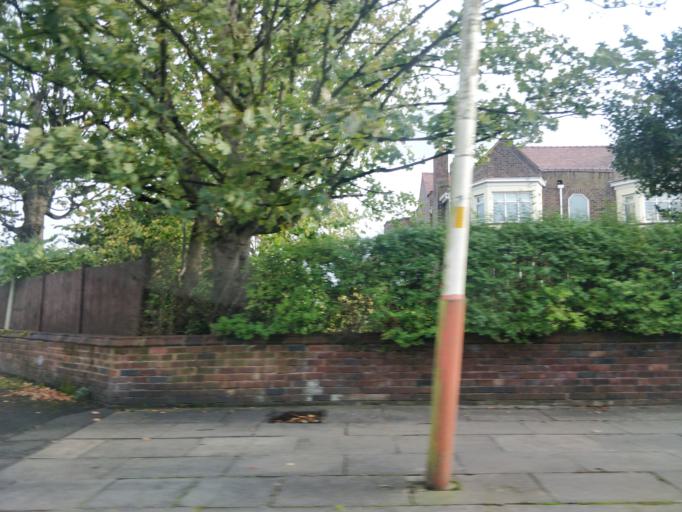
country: GB
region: England
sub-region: Sefton
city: Southport
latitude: 53.6550
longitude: -2.9934
